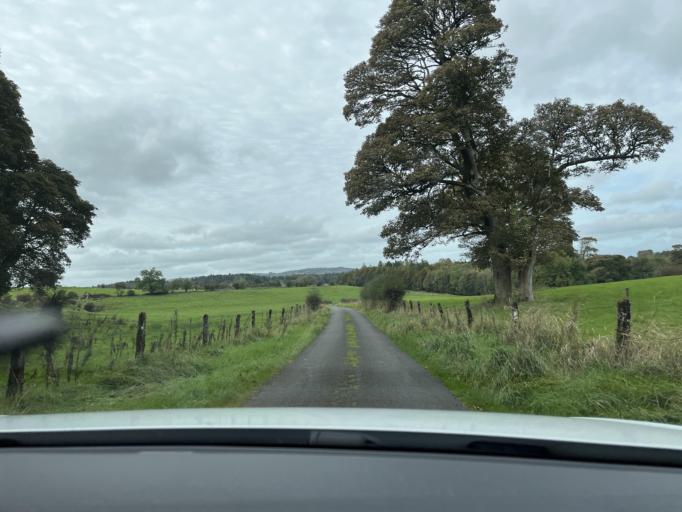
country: IE
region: Connaught
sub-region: Roscommon
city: Boyle
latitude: 53.9724
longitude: -8.2183
